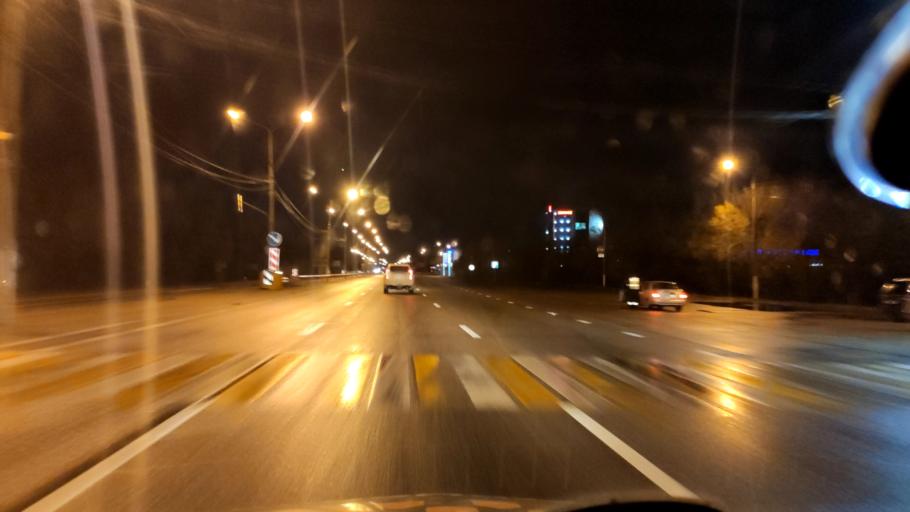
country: RU
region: Voronezj
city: Novaya Usman'
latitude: 51.6375
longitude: 39.3274
